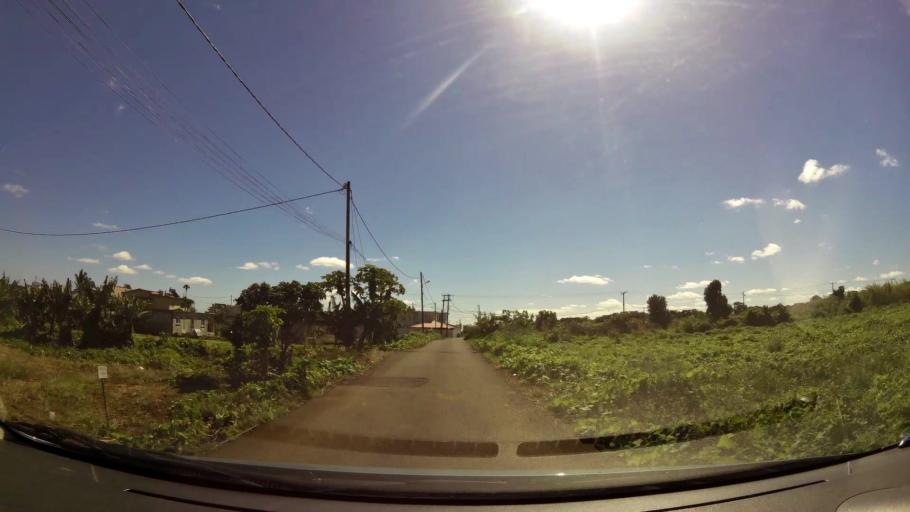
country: MU
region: Plaines Wilhems
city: Curepipe
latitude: -20.3337
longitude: 57.4905
